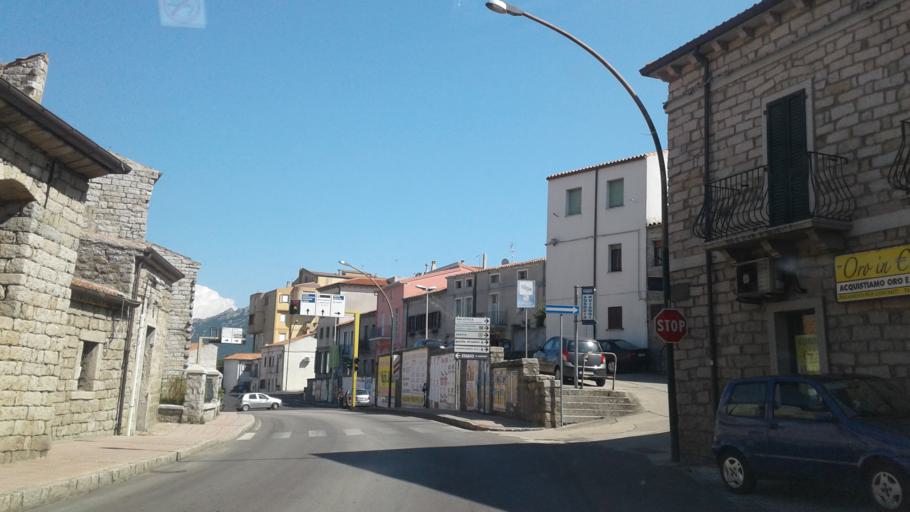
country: IT
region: Sardinia
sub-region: Provincia di Olbia-Tempio
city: Tempio Pausania
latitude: 40.9022
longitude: 9.1059
